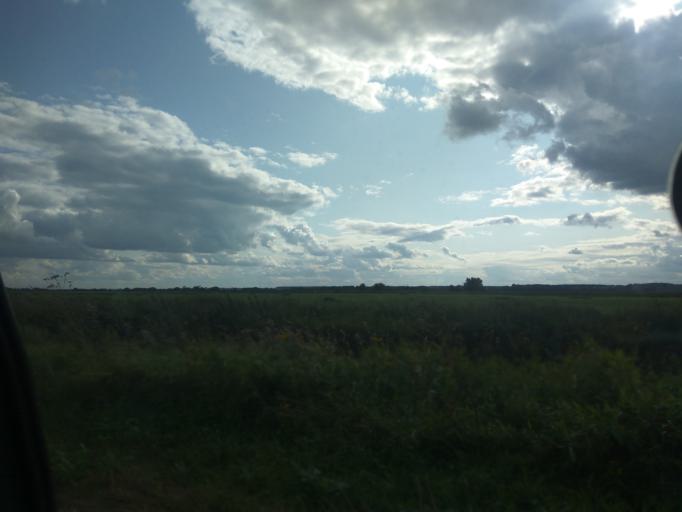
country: RU
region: Moskovskaya
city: Ramenskoye
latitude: 55.5051
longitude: 38.2238
